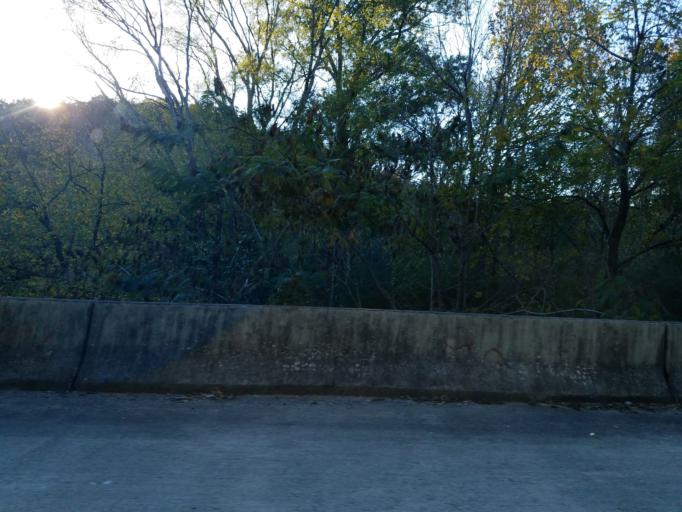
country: US
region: Georgia
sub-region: Bartow County
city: Euharlee
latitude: 34.2307
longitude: -84.9406
